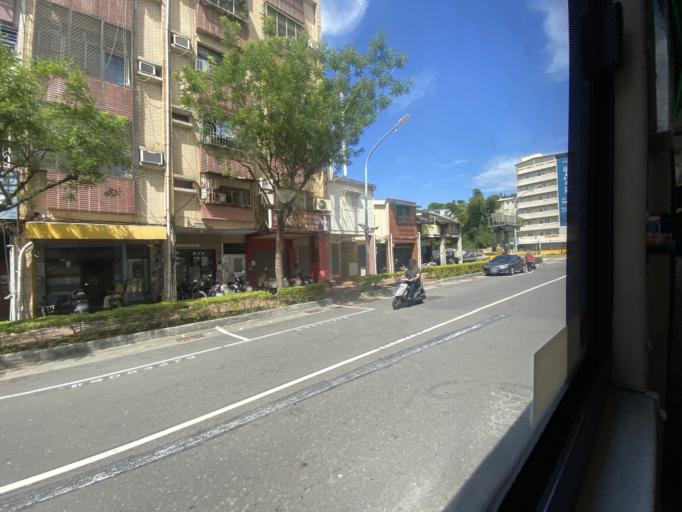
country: TW
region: Kaohsiung
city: Kaohsiung
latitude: 22.6258
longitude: 120.2792
